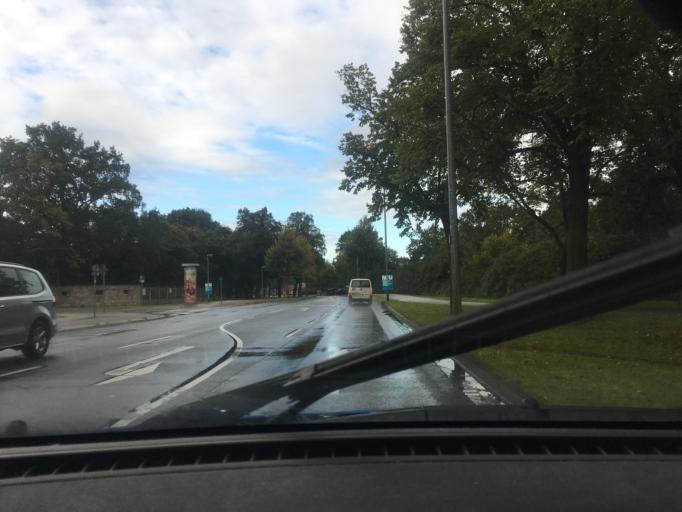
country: DE
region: Lower Saxony
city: Langenhagen
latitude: 52.4159
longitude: 9.7934
